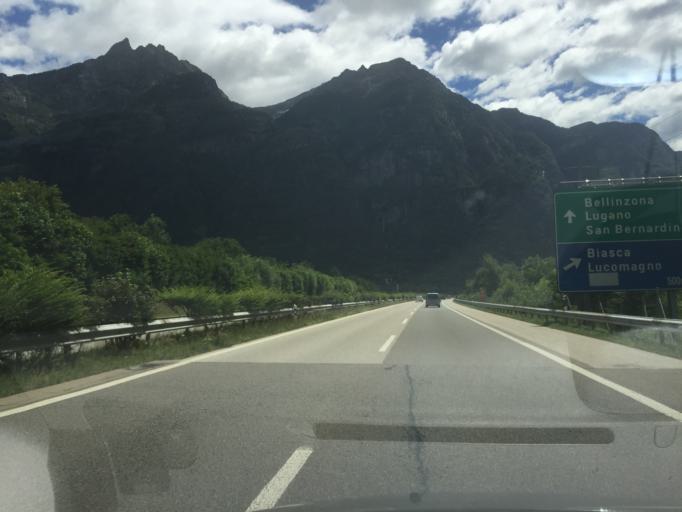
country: CH
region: Ticino
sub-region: Riviera District
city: Biasca
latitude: 46.3607
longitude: 8.9458
